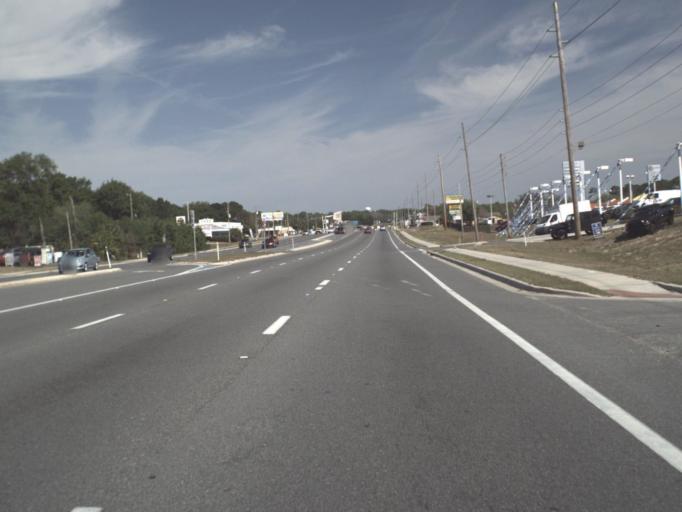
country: US
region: Florida
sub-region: Lake County
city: Fruitland Park
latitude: 28.8459
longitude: -81.8984
